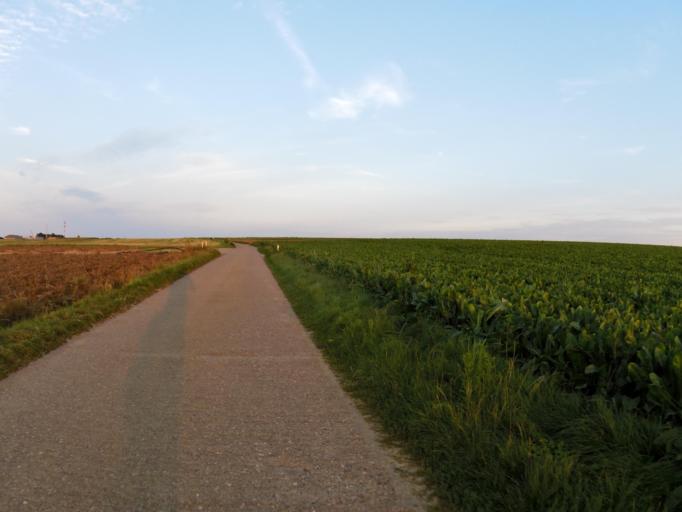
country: BE
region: Wallonia
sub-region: Province de Liege
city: Juprelle
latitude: 50.7654
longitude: 5.5425
